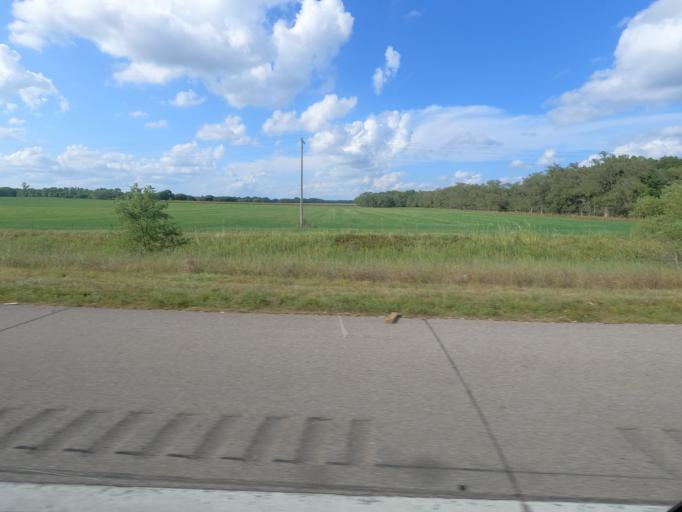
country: US
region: Kansas
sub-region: Shawnee County
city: Rossville
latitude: 39.0591
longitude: -96.0275
